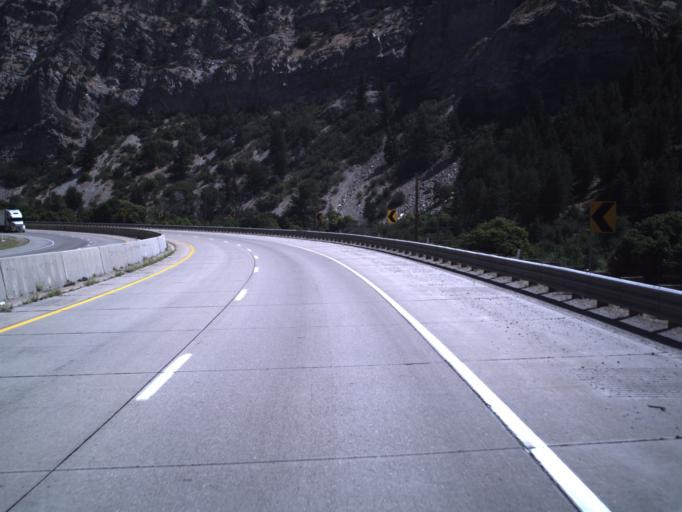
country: US
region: Utah
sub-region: Morgan County
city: Morgan
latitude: 41.0529
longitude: -111.5972
